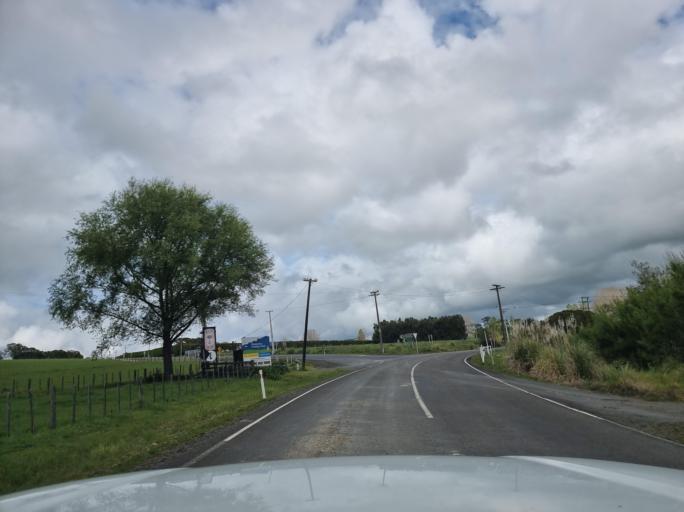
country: NZ
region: Northland
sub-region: Whangarei
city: Ruakaka
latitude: -36.1252
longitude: 174.1882
